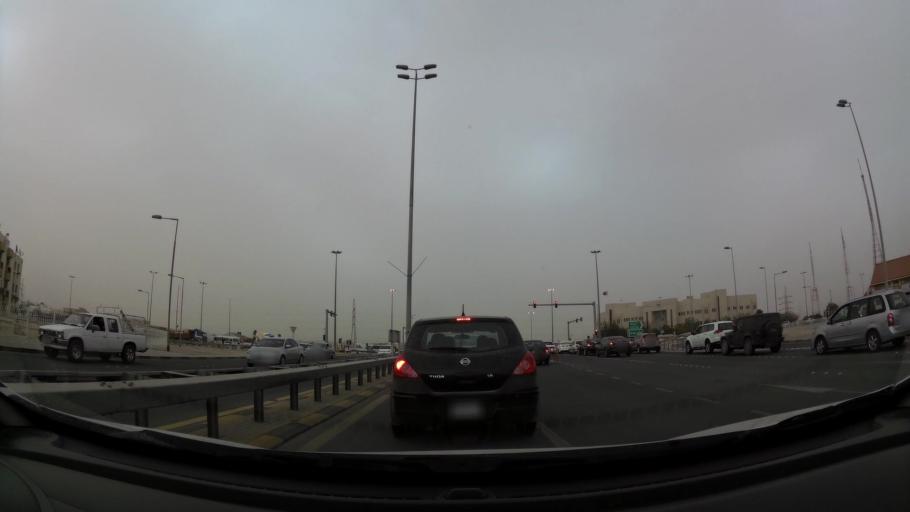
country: BH
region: Northern
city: Madinat `Isa
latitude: 26.1625
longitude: 50.5626
